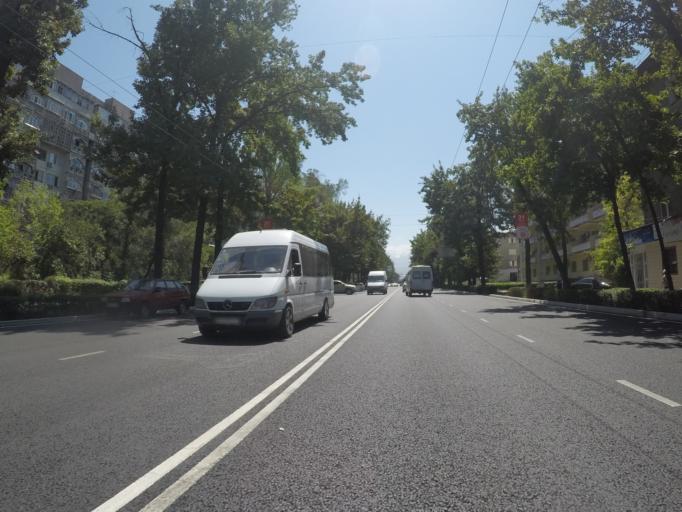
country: KG
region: Chuy
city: Bishkek
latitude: 42.8719
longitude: 74.5878
